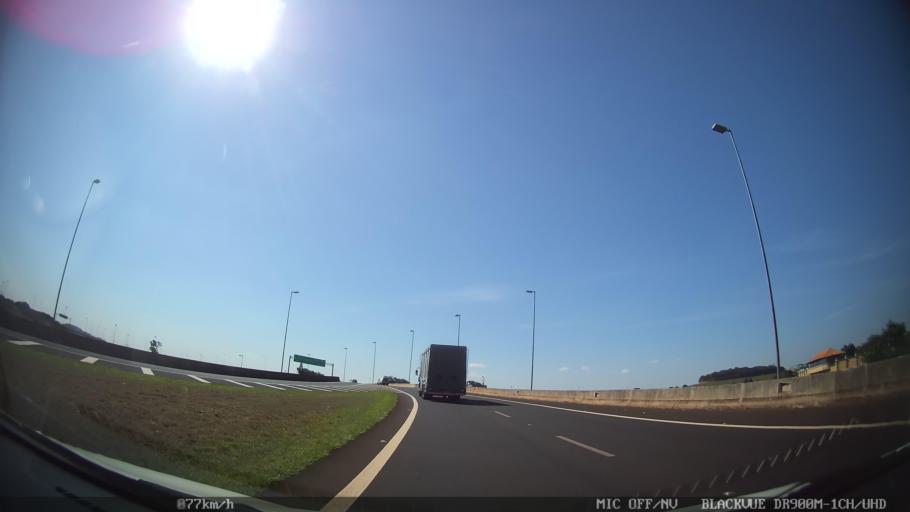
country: BR
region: Sao Paulo
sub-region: Ribeirao Preto
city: Ribeirao Preto
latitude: -21.2070
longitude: -47.7561
